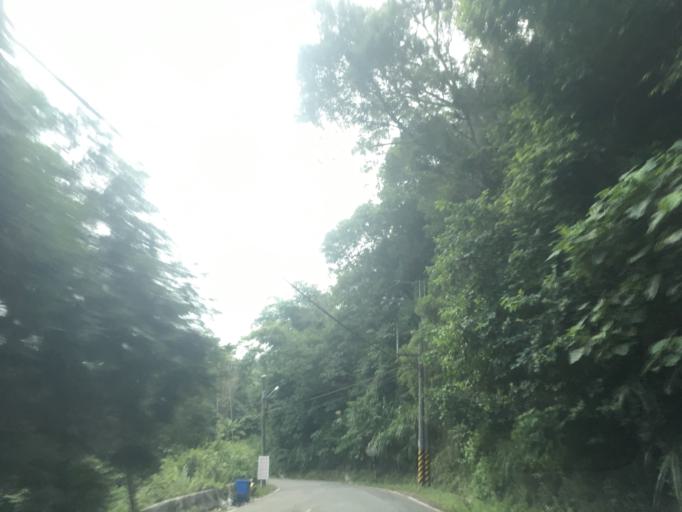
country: TW
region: Taiwan
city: Fengyuan
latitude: 24.1909
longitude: 120.7687
